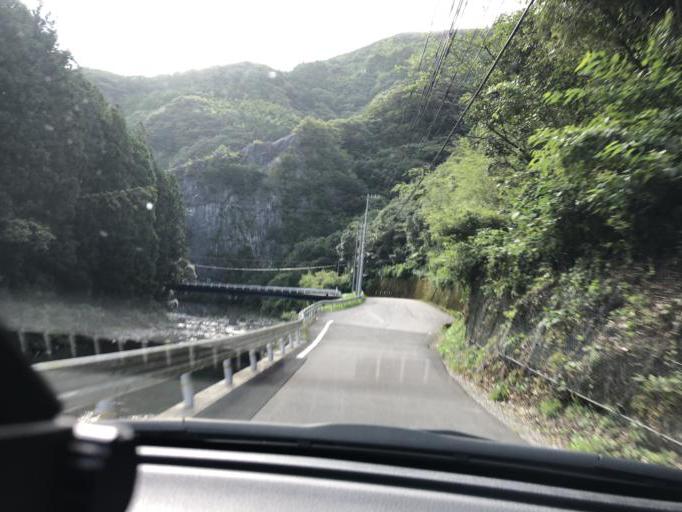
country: JP
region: Kochi
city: Kochi-shi
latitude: 33.6286
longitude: 133.5081
